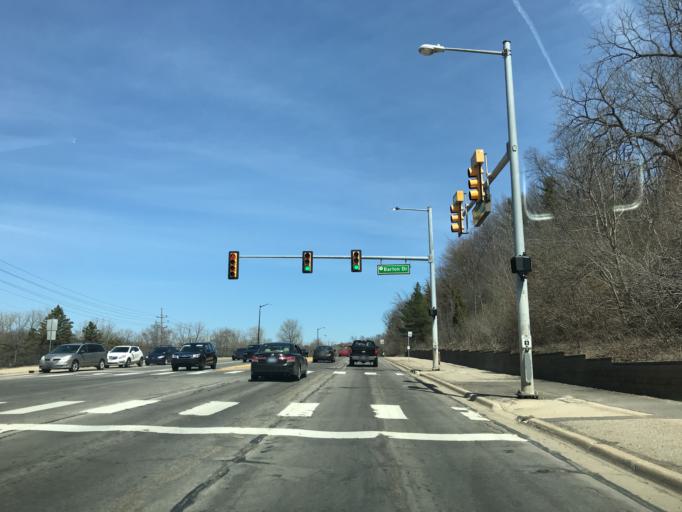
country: US
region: Michigan
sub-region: Washtenaw County
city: Ann Arbor
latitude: 42.2962
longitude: -83.7309
